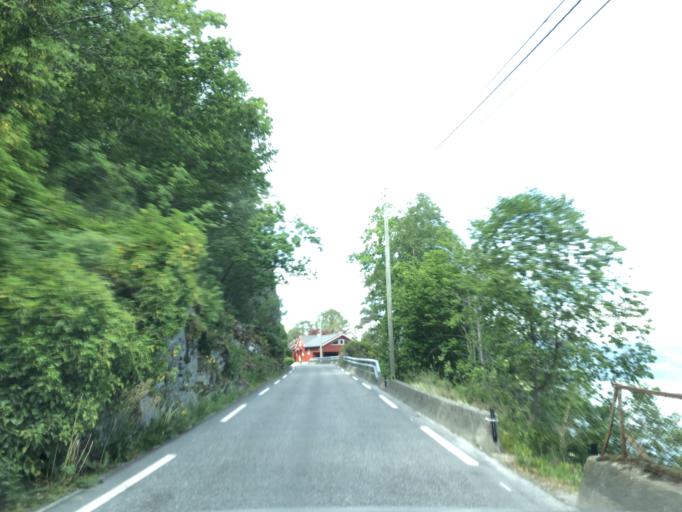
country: NO
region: Hordaland
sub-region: Jondal
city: Jondal
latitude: 60.3049
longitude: 6.2800
